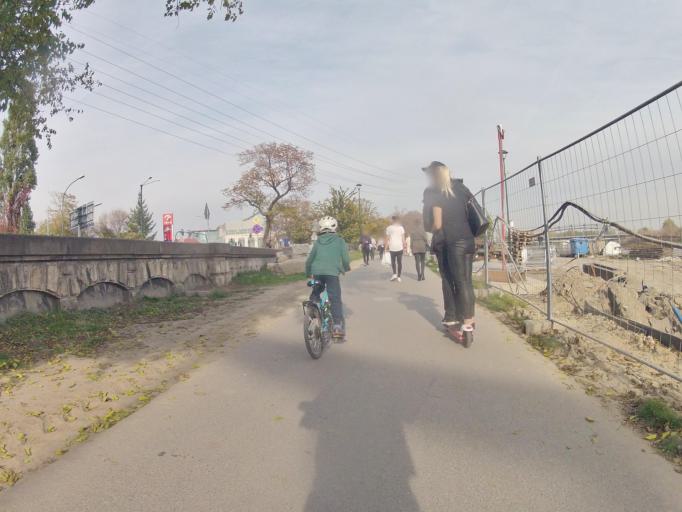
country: PL
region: Lesser Poland Voivodeship
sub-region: Krakow
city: Krakow
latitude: 50.0508
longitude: 19.9544
